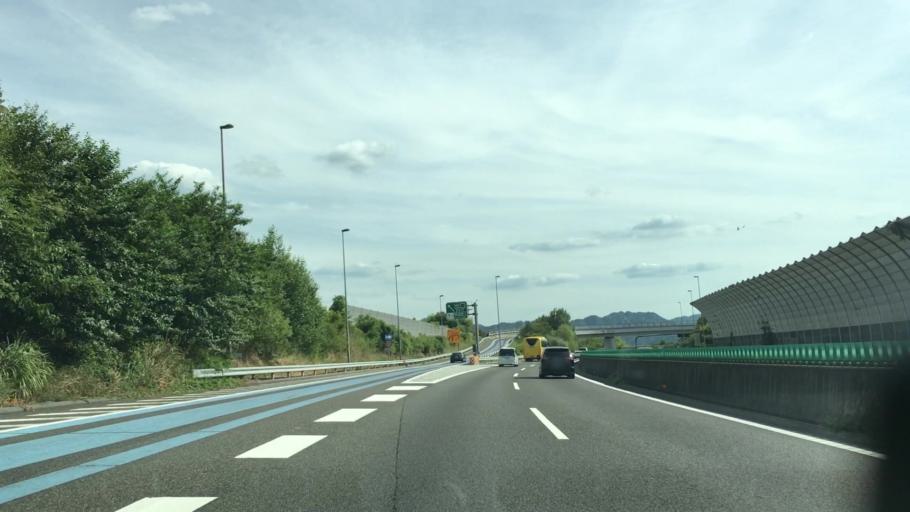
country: JP
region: Shiga Prefecture
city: Kusatsu
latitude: 34.9761
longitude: 135.9618
